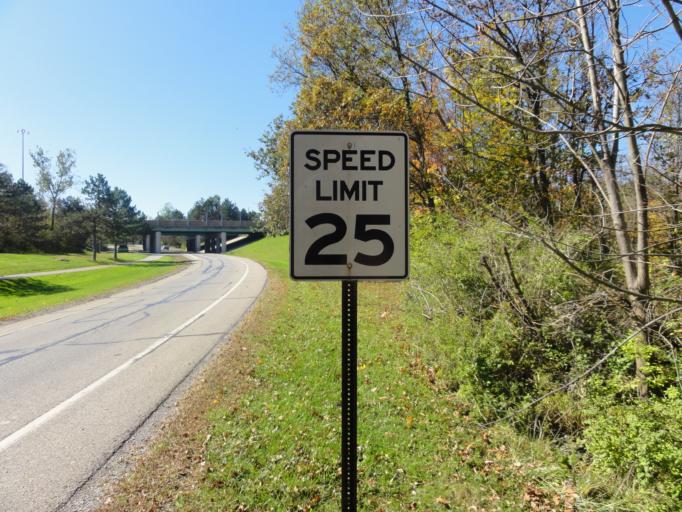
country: US
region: Ohio
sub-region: Cuyahoga County
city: Middleburg Heights
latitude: 41.3631
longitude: -81.8197
